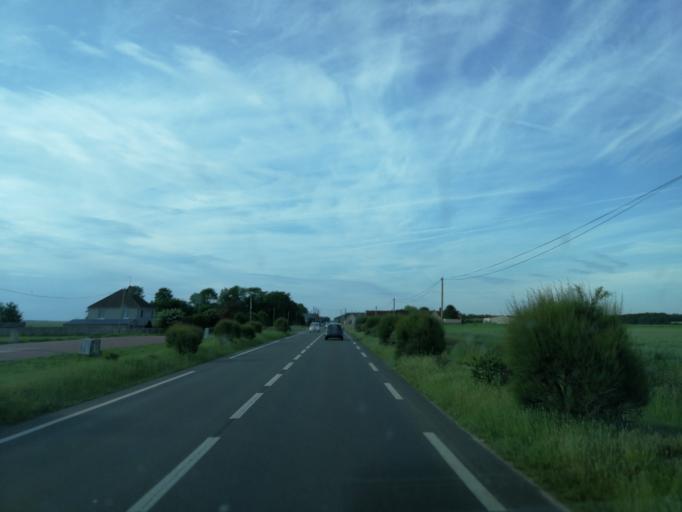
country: FR
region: Centre
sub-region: Departement d'Eure-et-Loir
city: Dammarie
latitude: 48.3225
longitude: 1.4309
